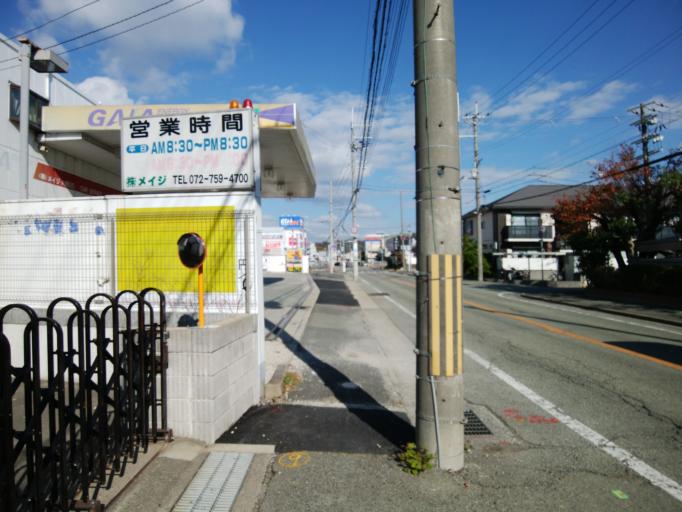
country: JP
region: Osaka
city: Ikeda
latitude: 34.8372
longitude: 135.4208
